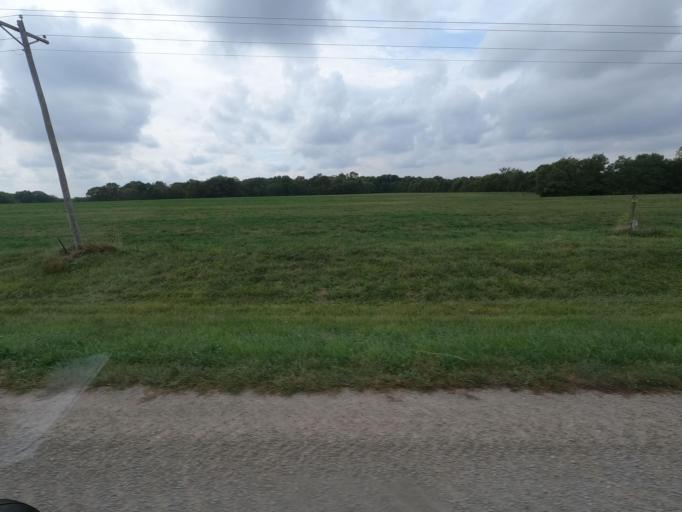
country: US
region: Iowa
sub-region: Wapello County
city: Ottumwa
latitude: 40.9537
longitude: -92.2365
